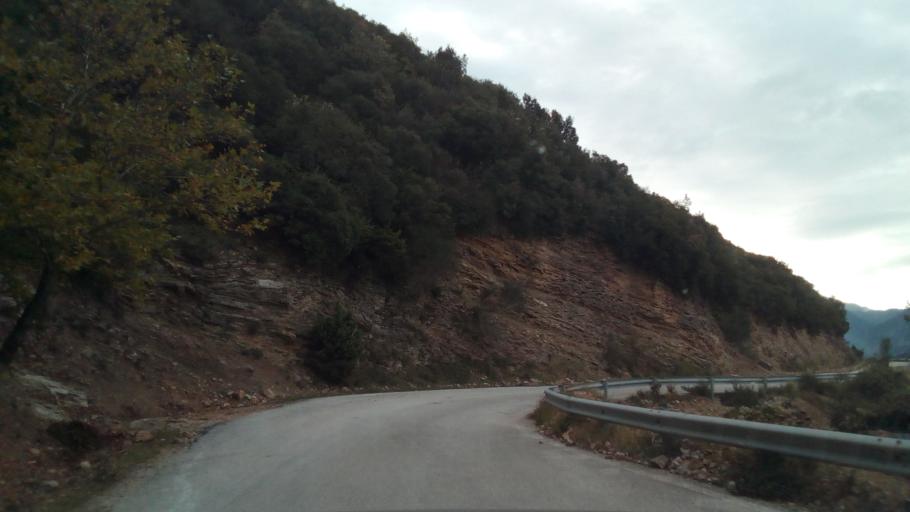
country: GR
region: West Greece
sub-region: Nomos Aitolias kai Akarnanias
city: Thermo
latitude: 38.5992
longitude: 21.8078
